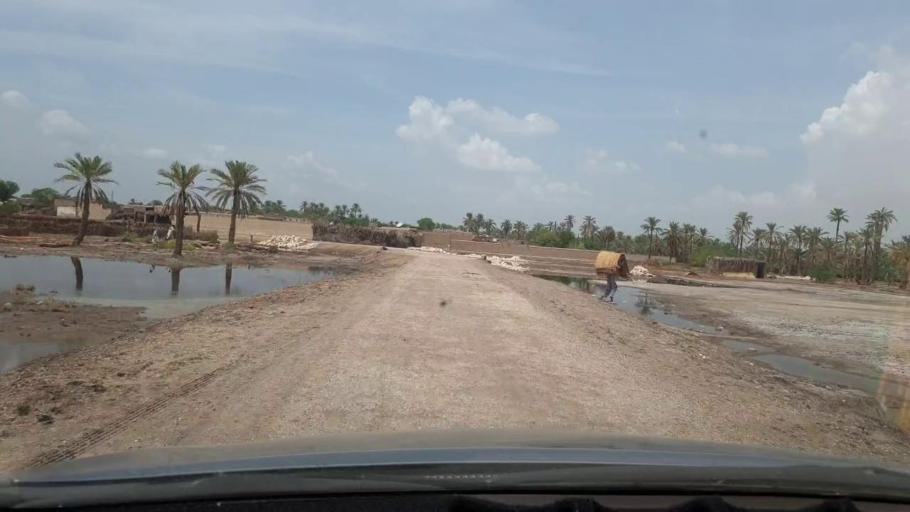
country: PK
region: Sindh
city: Khairpur
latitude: 27.4568
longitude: 68.8239
